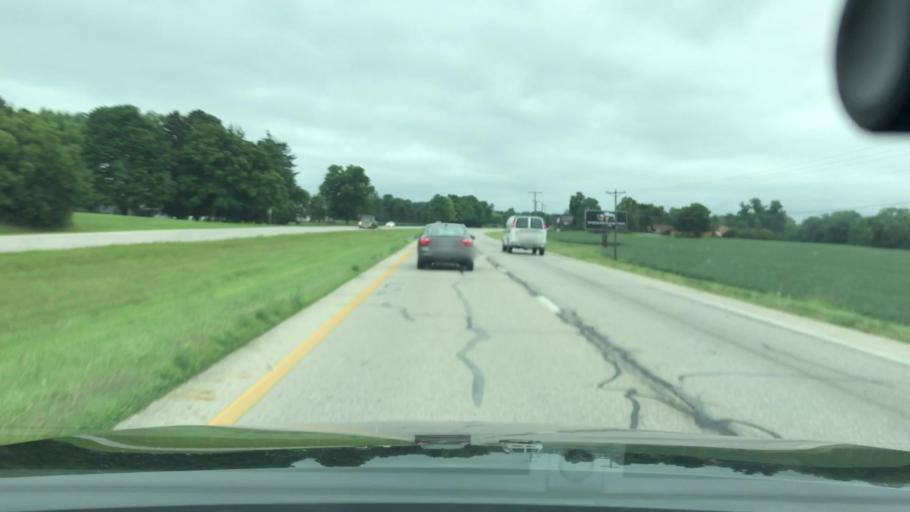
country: US
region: Ohio
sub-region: Pickaway County
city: Logan Elm Village
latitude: 39.5053
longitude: -82.9739
